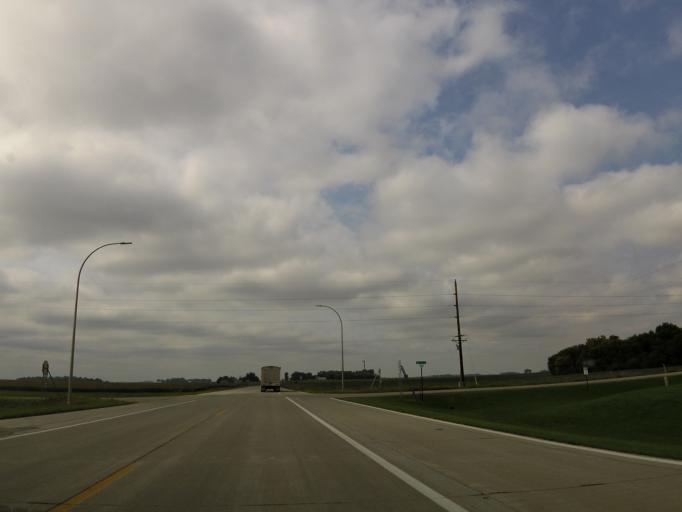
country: US
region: Minnesota
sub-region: Lac qui Parle County
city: Dawson
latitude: 44.9354
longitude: -95.9204
